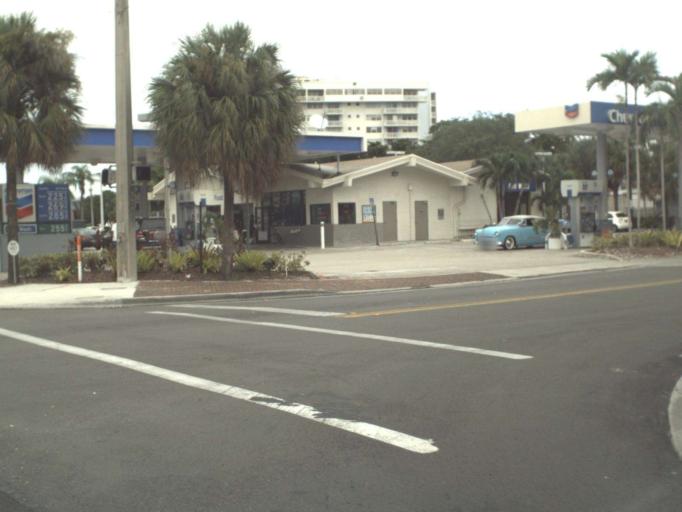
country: US
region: Florida
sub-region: Miami-Dade County
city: Biscayne Park
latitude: 25.8962
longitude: -80.1616
